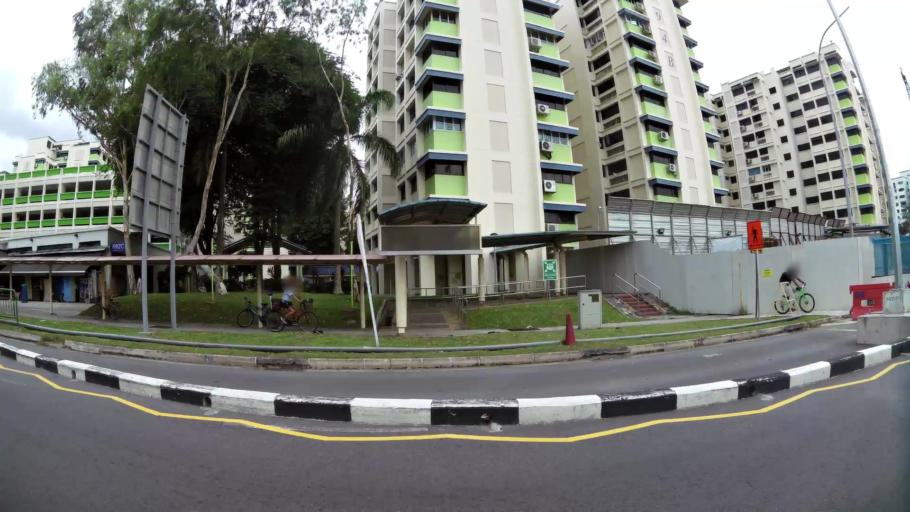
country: MY
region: Johor
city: Johor Bahru
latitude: 1.4364
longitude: 103.7890
